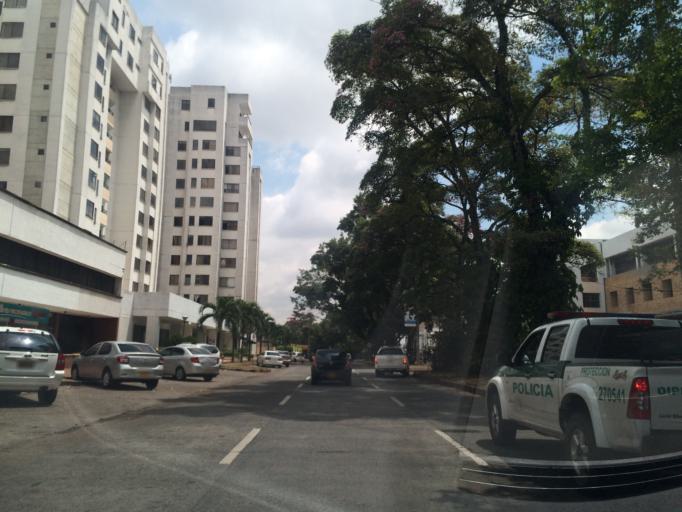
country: CO
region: Valle del Cauca
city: Cali
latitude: 3.4141
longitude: -76.5408
